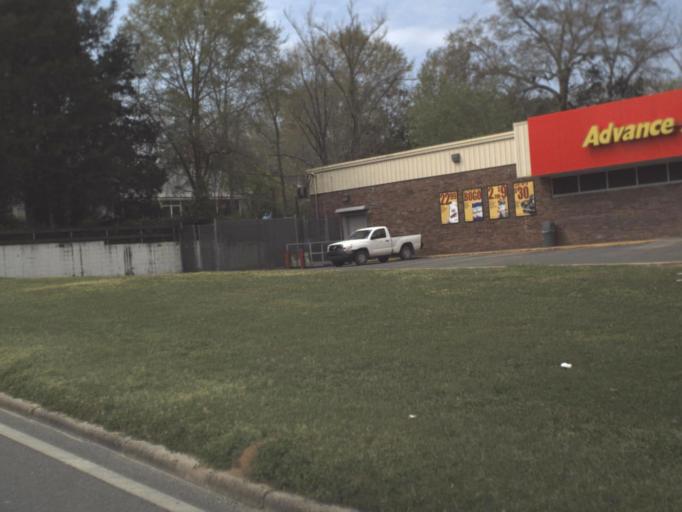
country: US
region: Florida
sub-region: Holmes County
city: Bonifay
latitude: 30.8001
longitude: -85.6794
